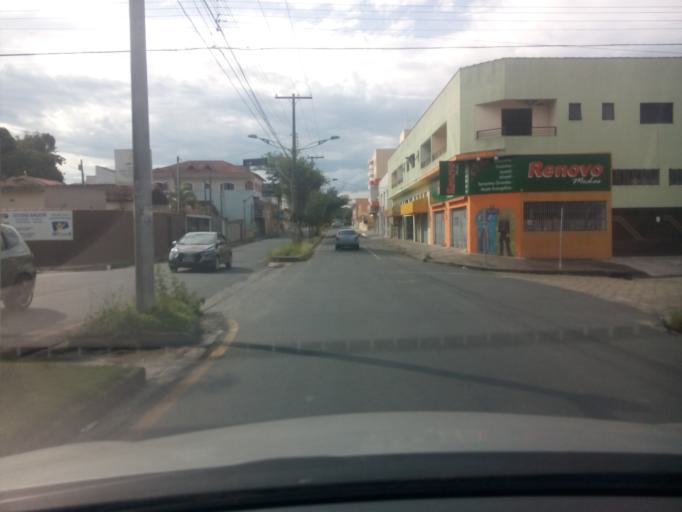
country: BR
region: Sao Paulo
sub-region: Peruibe
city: Peruibe
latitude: -24.3202
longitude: -46.9979
